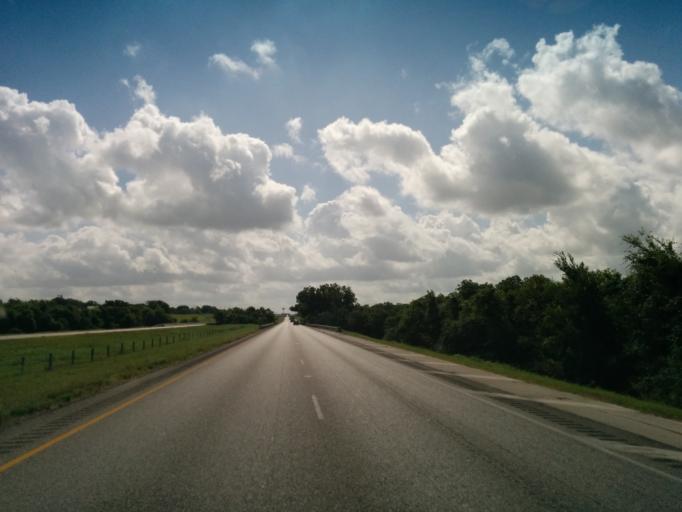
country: US
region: Texas
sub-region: Fayette County
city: Schulenburg
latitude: 29.6894
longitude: -96.9409
